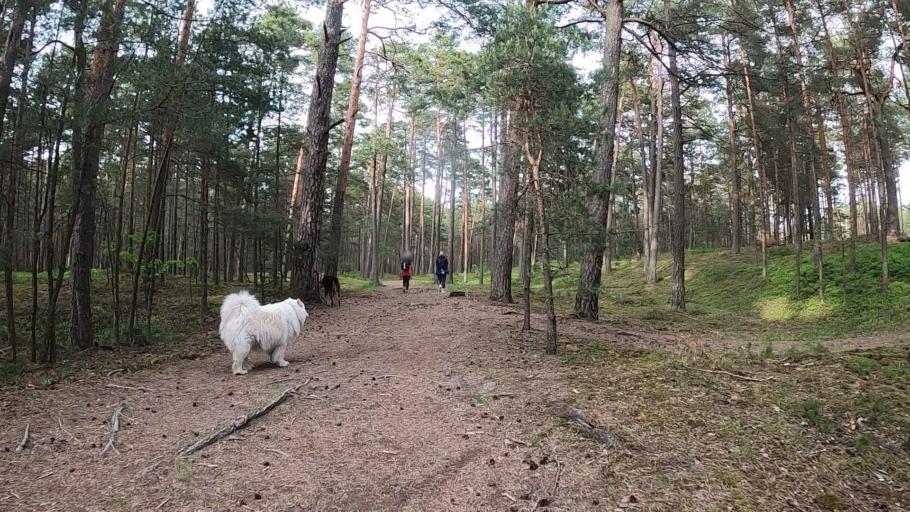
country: LV
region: Riga
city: Jaunciems
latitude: 57.0872
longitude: 24.1548
